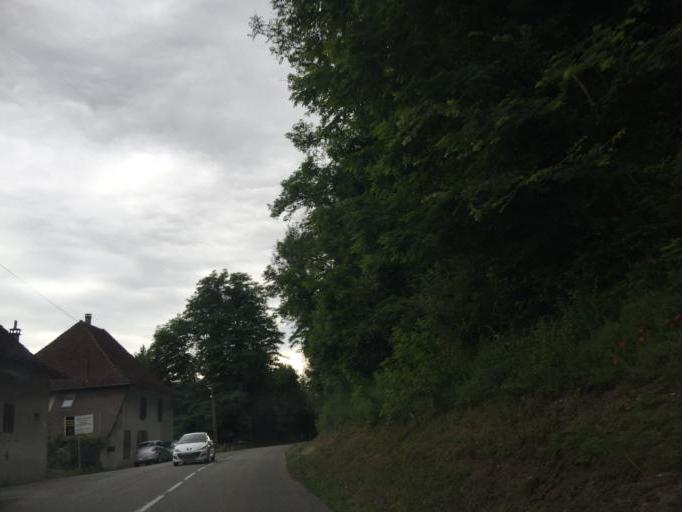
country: FR
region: Rhone-Alpes
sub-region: Departement de la Savoie
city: Le Pont-de-Beauvoisin
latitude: 45.5471
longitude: 5.6772
